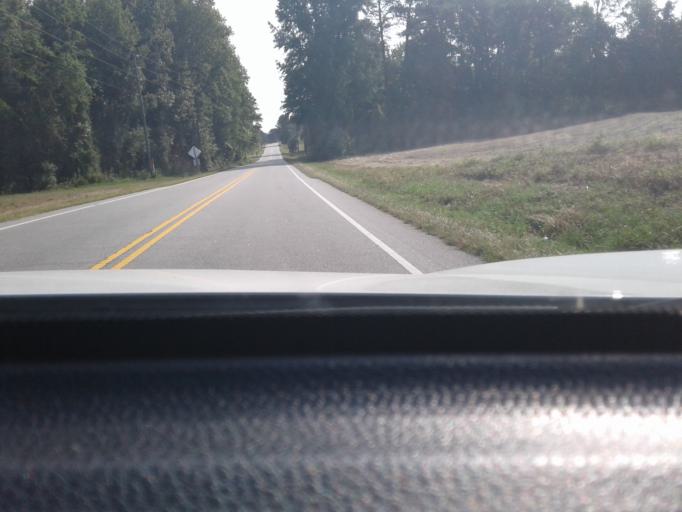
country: US
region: North Carolina
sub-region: Johnston County
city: Benson
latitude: 35.4181
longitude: -78.5381
